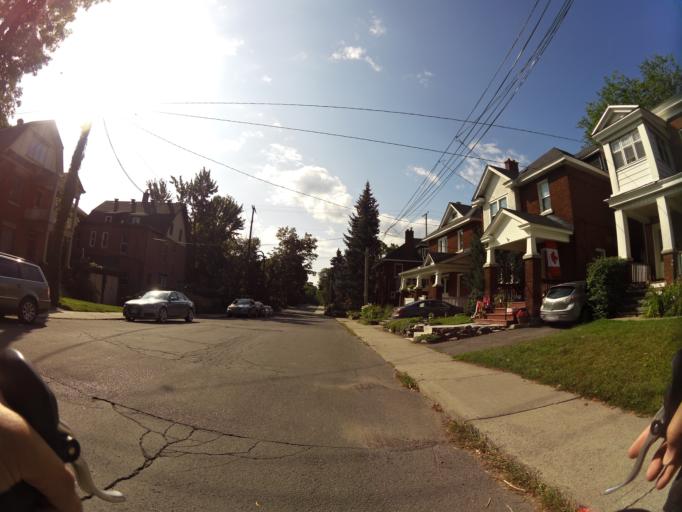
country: CA
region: Ontario
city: Ottawa
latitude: 45.3990
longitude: -75.6899
